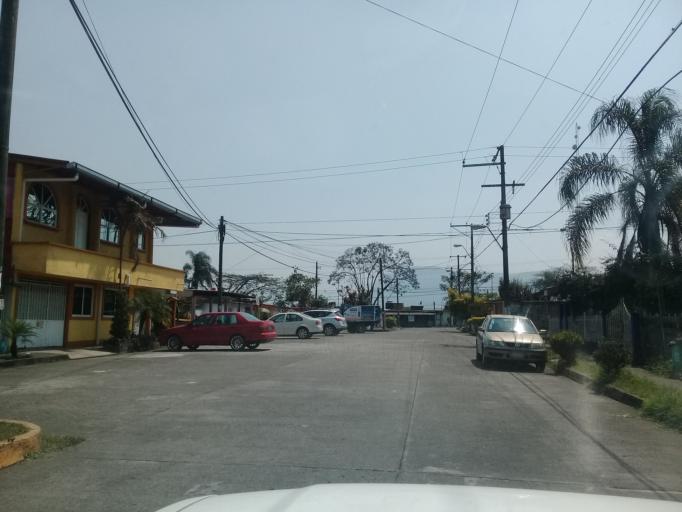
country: MX
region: Veracruz
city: Ixtac Zoquitlan
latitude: 18.8765
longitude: -97.0532
